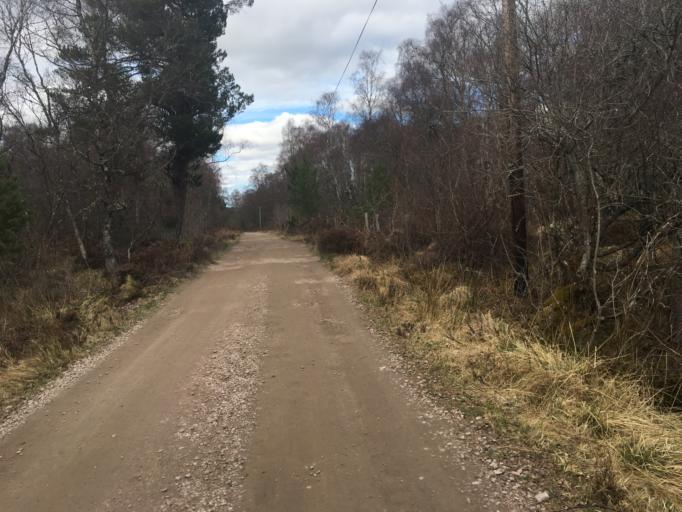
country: GB
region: Scotland
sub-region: Highland
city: Aviemore
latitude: 57.1648
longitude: -3.8121
